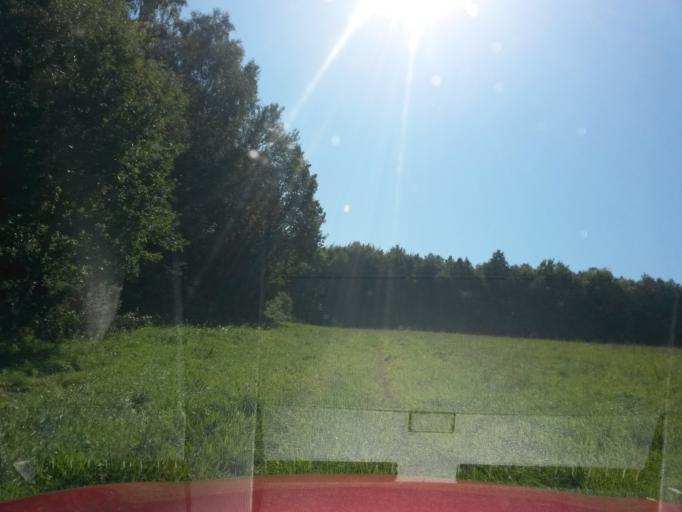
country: SK
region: Presovsky
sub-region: Okres Presov
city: Presov
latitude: 48.9856
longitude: 21.1486
